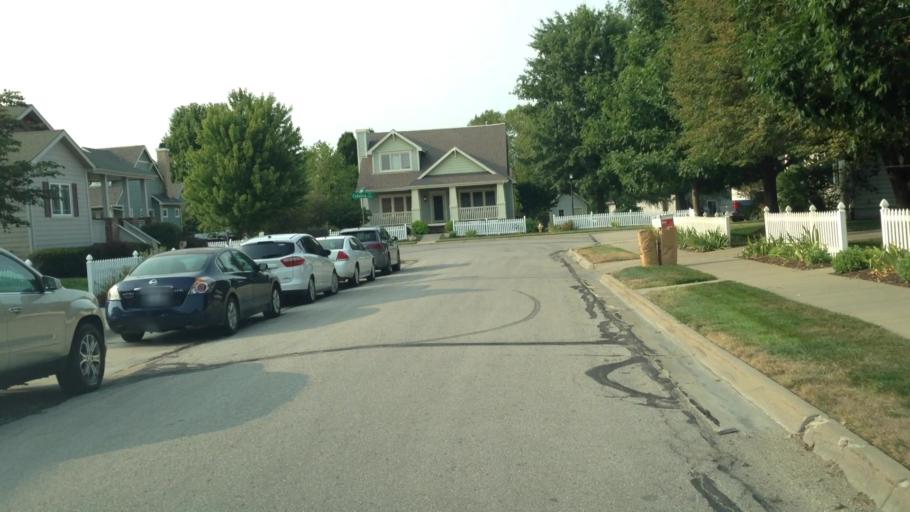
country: US
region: Kansas
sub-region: Douglas County
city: Lawrence
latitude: 38.9748
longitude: -95.2948
